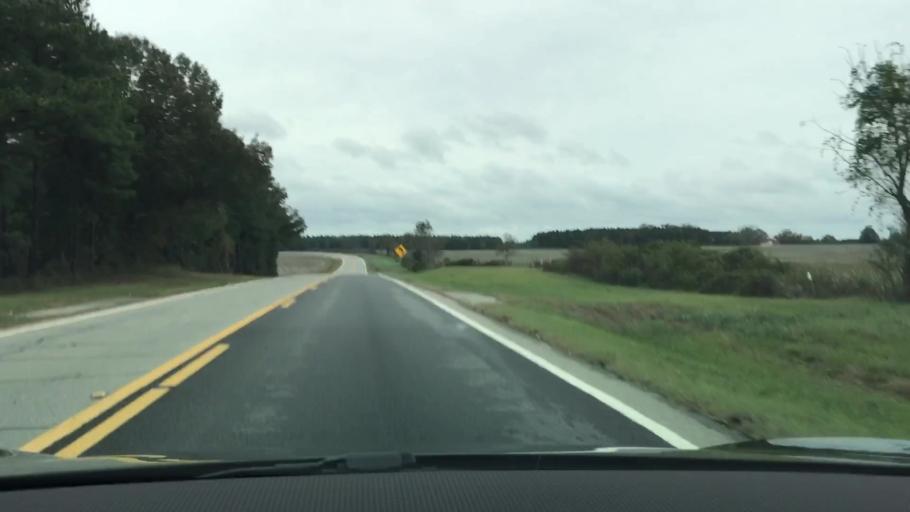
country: US
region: Georgia
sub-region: Warren County
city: Warrenton
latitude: 33.3613
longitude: -82.5969
